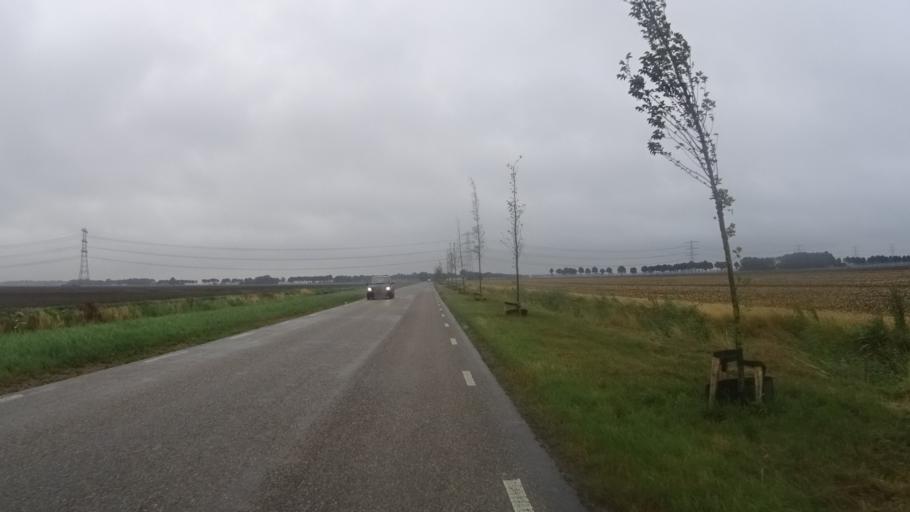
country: NL
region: Groningen
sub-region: Gemeente Veendam
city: Veendam
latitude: 53.1918
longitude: 6.9077
